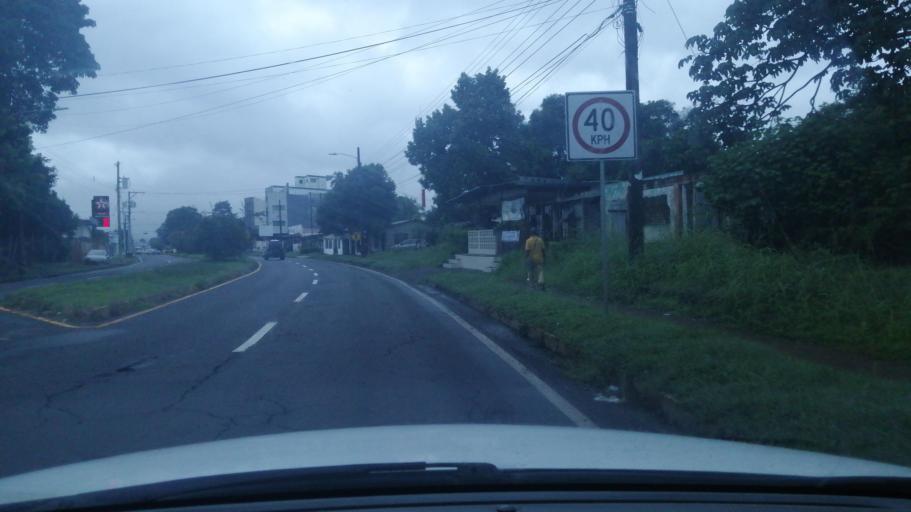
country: PA
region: Chiriqui
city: David
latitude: 8.4188
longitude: -82.4327
